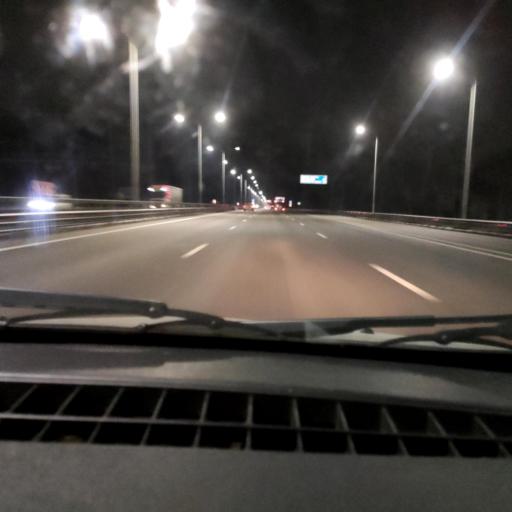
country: RU
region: Voronezj
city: Podgornoye
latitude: 51.8384
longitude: 39.2211
